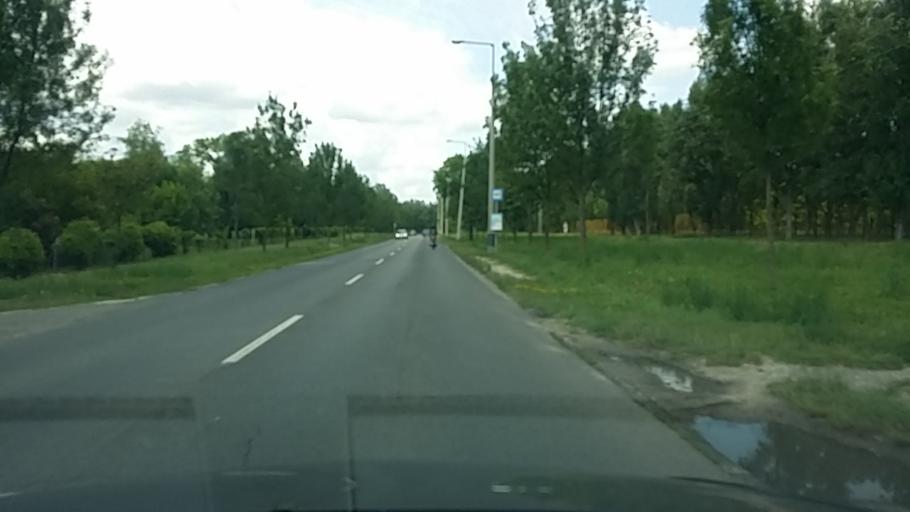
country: HU
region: Bacs-Kiskun
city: Kecskemet
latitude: 46.9096
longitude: 19.6525
